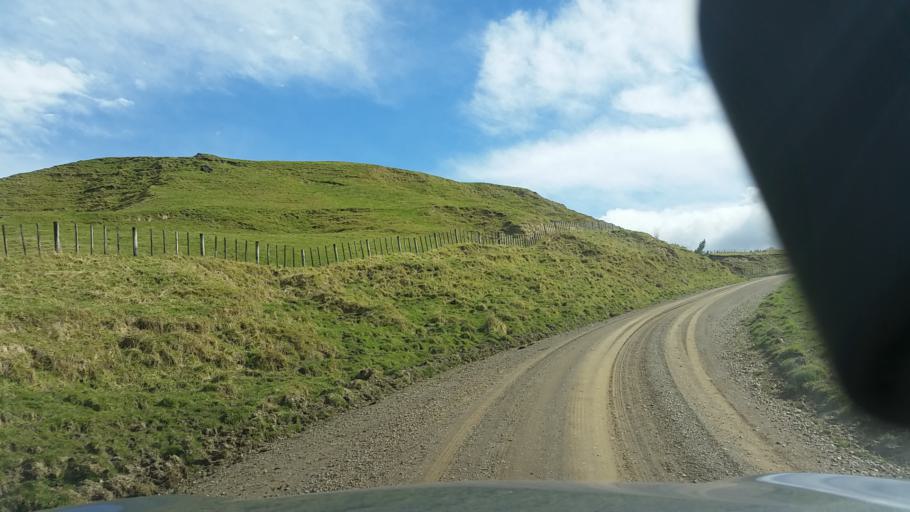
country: NZ
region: Hawke's Bay
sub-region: Napier City
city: Napier
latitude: -39.2117
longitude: 176.9664
